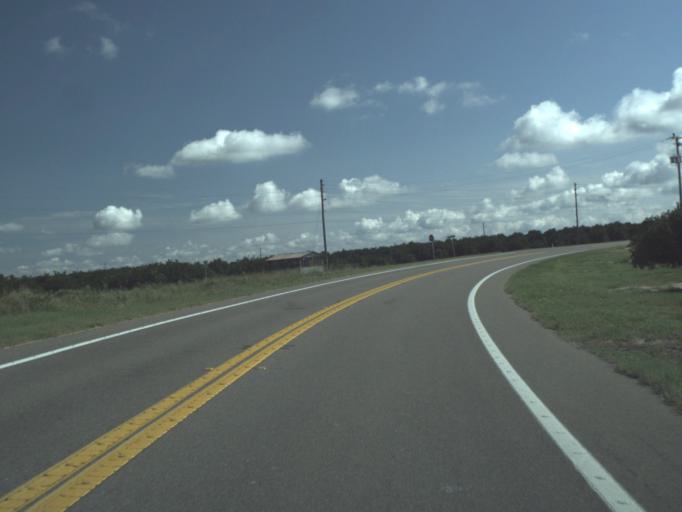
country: US
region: Florida
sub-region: Polk County
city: Babson Park
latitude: 27.8135
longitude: -81.5381
